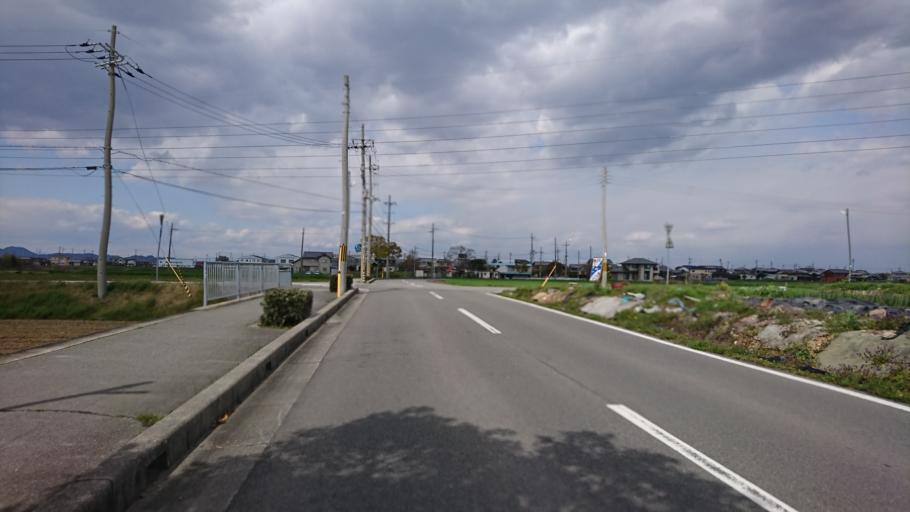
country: JP
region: Hyogo
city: Kakogawacho-honmachi
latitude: 34.7571
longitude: 134.9072
